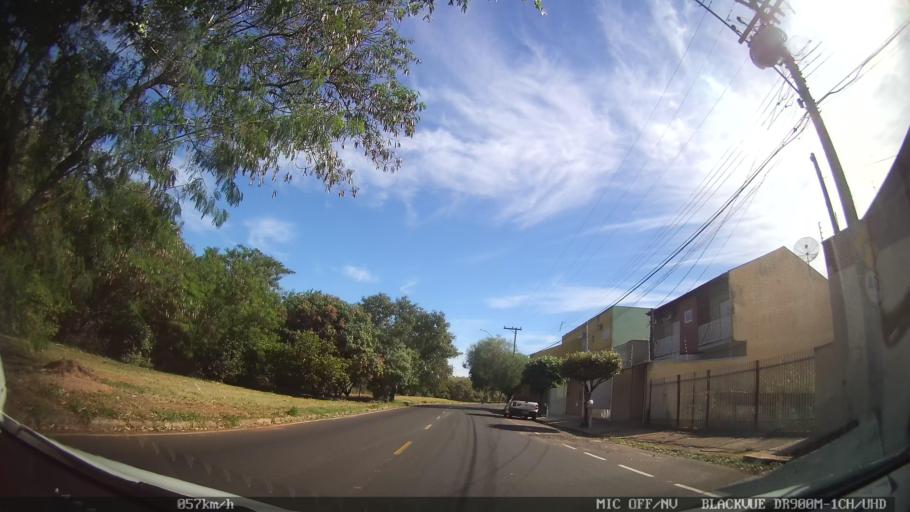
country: BR
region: Sao Paulo
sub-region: Sao Jose Do Rio Preto
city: Sao Jose do Rio Preto
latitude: -20.8504
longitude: -49.3650
